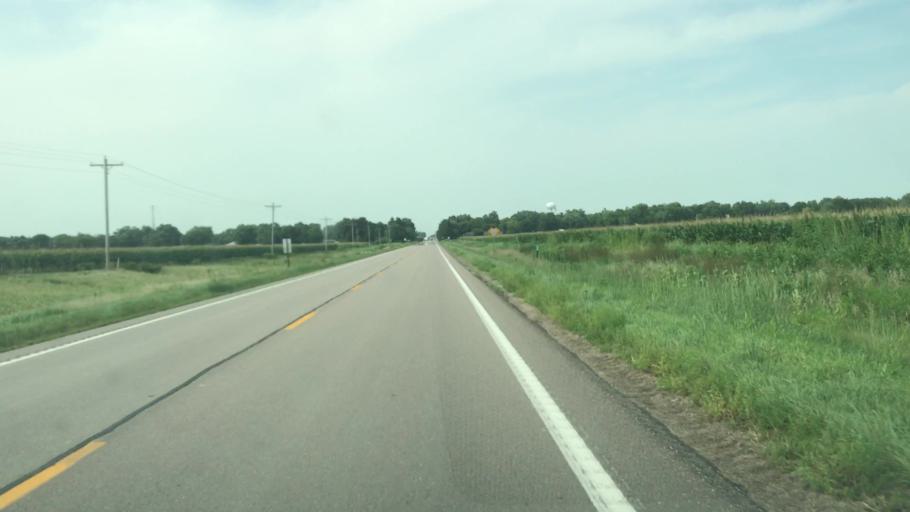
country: US
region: Nebraska
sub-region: Hall County
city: Wood River
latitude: 40.9917
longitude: -98.6075
